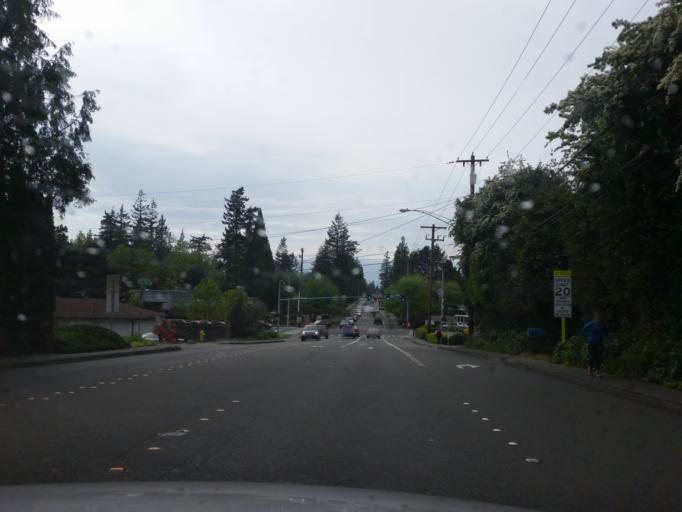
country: US
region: Washington
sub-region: Snohomish County
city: Alderwood Manor
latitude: 47.8283
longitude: -122.2905
